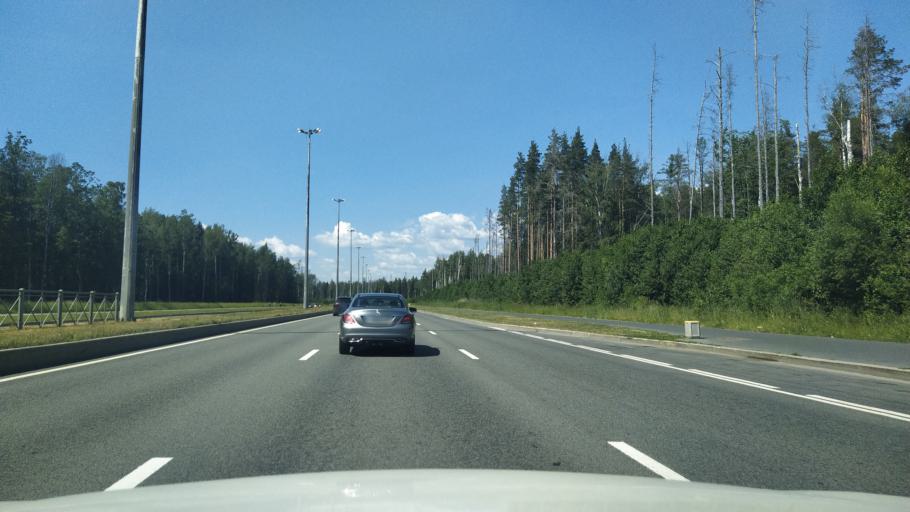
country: RU
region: St.-Petersburg
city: Levashovo
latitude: 60.0587
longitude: 30.2202
